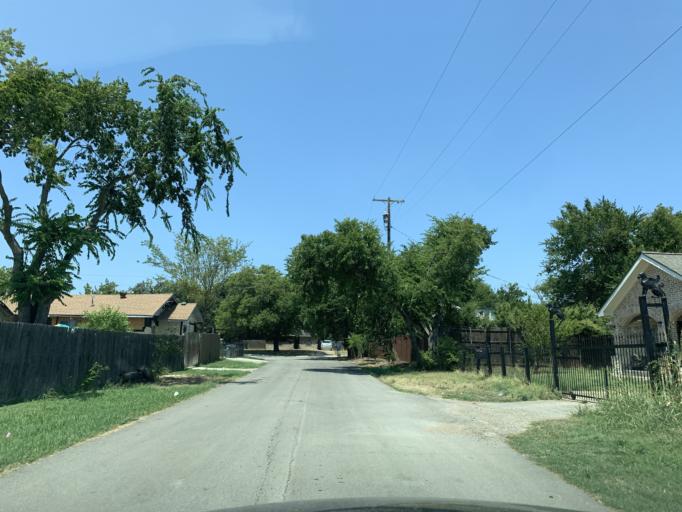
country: US
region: Texas
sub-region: Dallas County
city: Dallas
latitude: 32.6932
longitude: -96.8043
